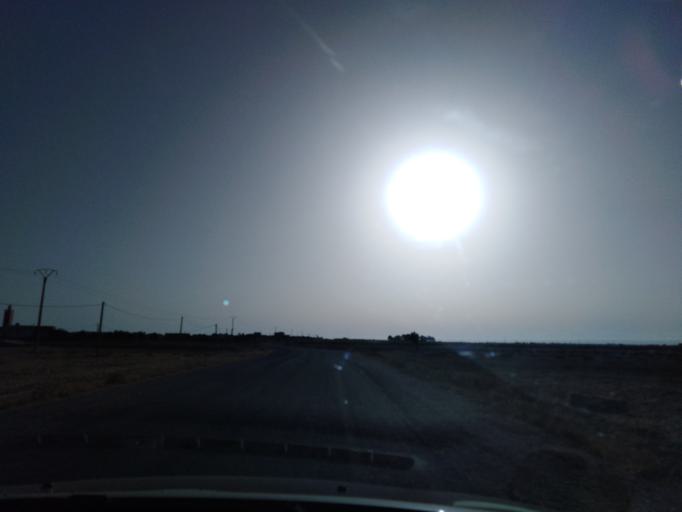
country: MA
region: Doukkala-Abda
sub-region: Safi
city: Safi
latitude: 32.4783
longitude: -8.8884
